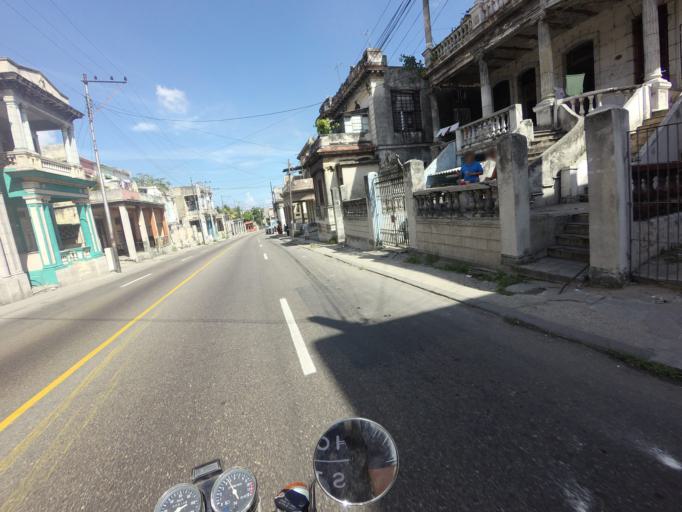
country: CU
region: La Habana
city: Diez de Octubre
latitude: 23.0992
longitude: -82.3623
